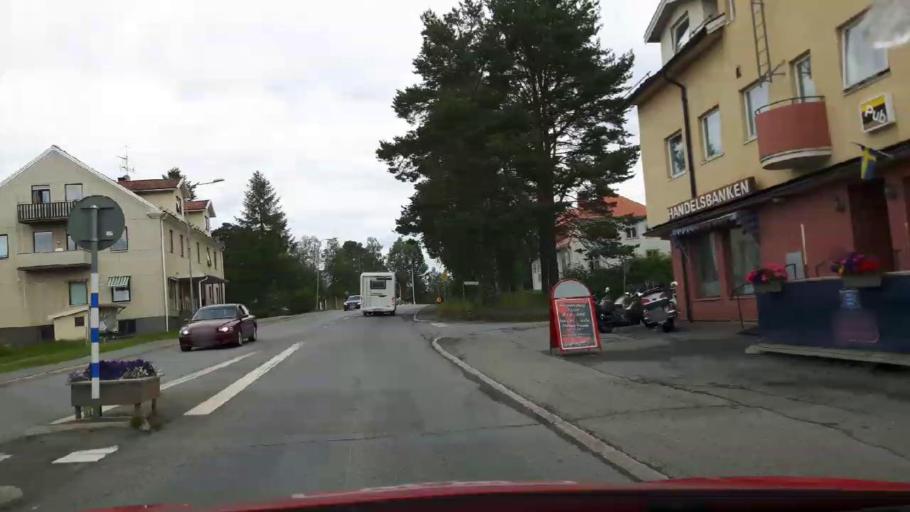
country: SE
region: Jaemtland
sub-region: Stroemsunds Kommun
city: Stroemsund
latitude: 63.5832
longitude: 15.3519
